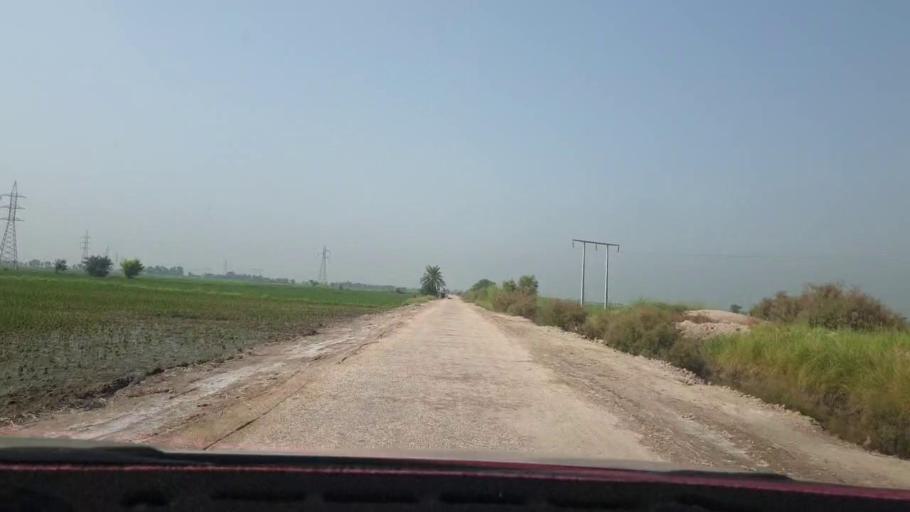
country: PK
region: Sindh
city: Nasirabad
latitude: 27.4266
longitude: 67.9434
